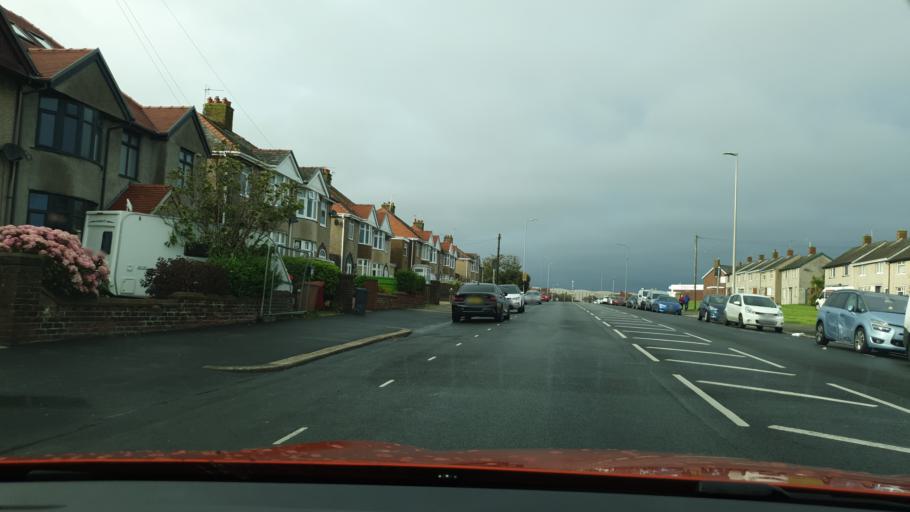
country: GB
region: England
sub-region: Cumbria
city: Barrow in Furness
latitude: 54.1012
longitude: -3.2509
